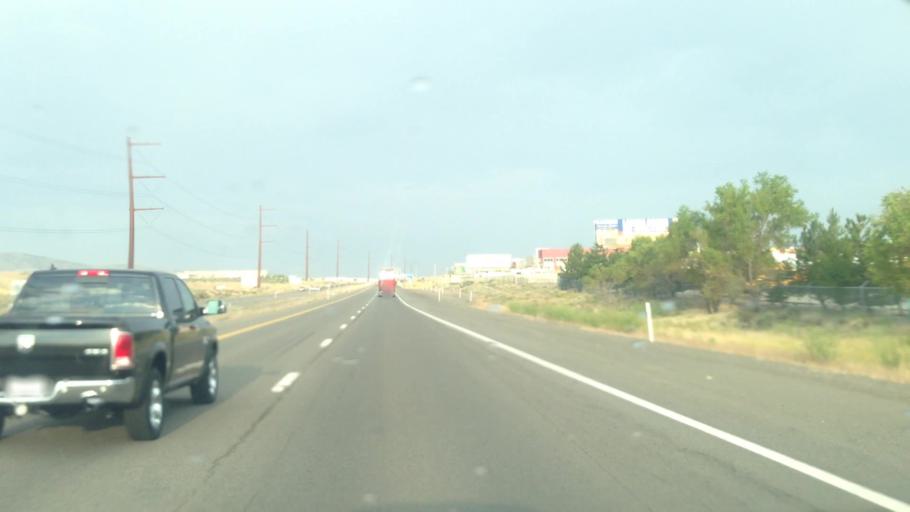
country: US
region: Nevada
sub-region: Washoe County
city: Lemmon Valley
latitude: 39.6164
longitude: -119.8696
